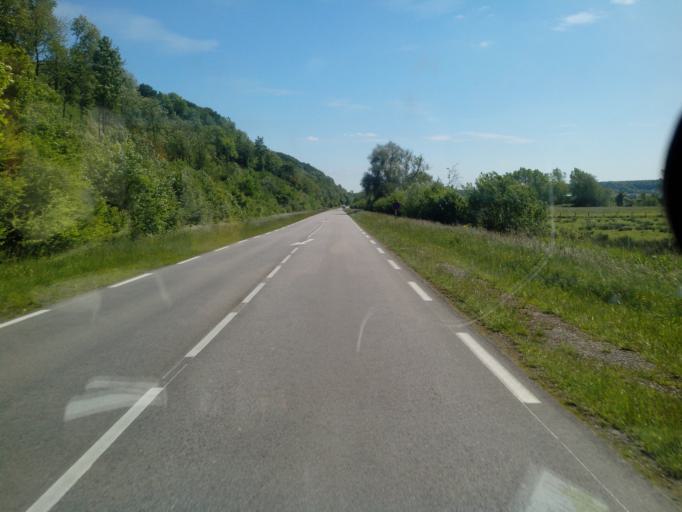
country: FR
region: Haute-Normandie
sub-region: Departement de la Seine-Maritime
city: Tancarville
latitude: 49.4311
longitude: 0.4242
